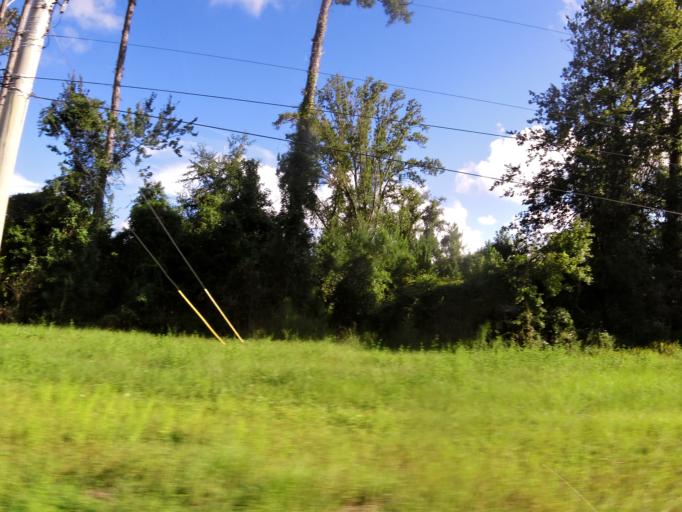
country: US
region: Georgia
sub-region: Camden County
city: Woodbine
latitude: 31.1050
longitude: -81.6832
